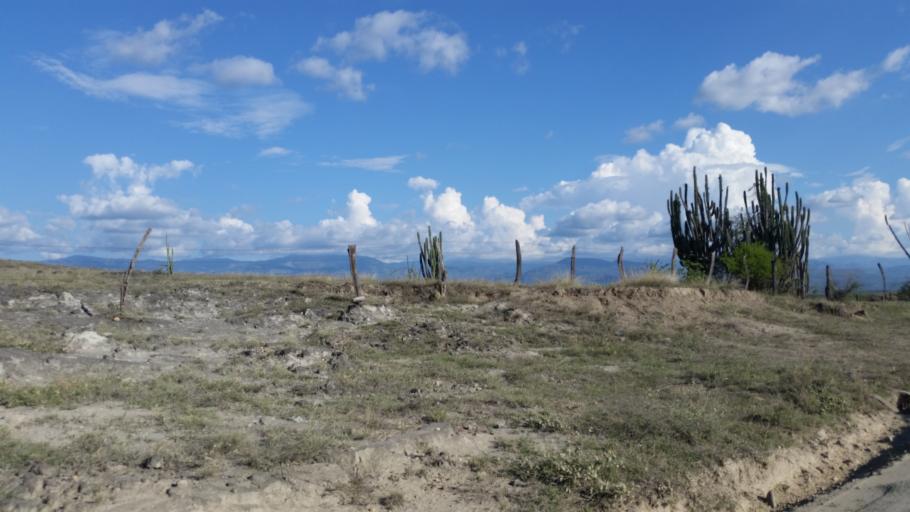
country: CO
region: Huila
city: Villavieja
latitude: 3.2251
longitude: -75.1264
